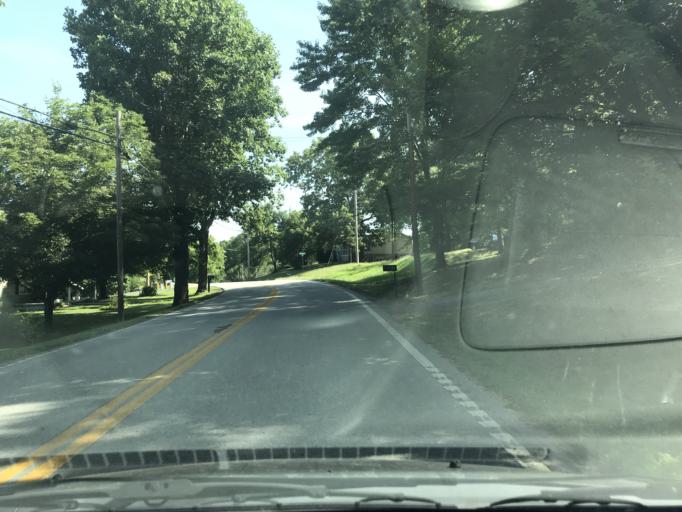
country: US
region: Tennessee
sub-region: Hamilton County
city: Lakesite
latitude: 35.1824
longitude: -85.0678
